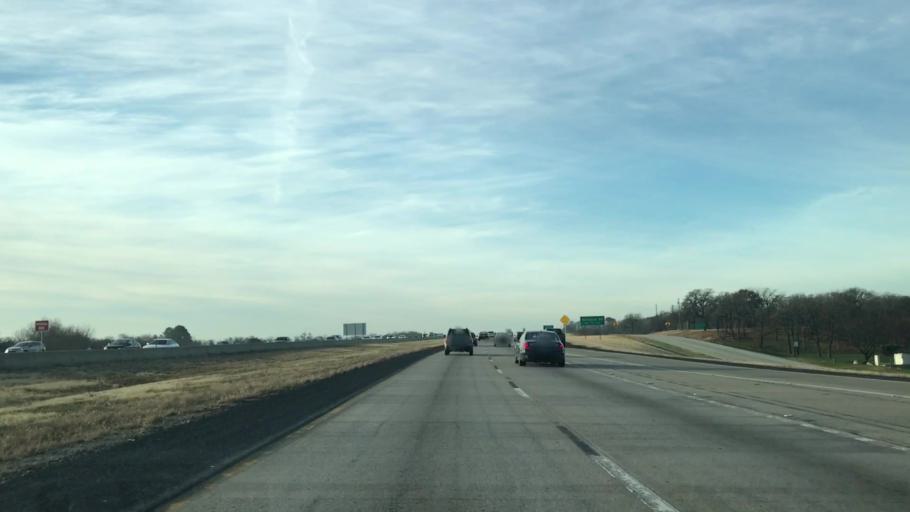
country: US
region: Texas
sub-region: Tarrant County
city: Euless
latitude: 32.8624
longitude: -97.1034
